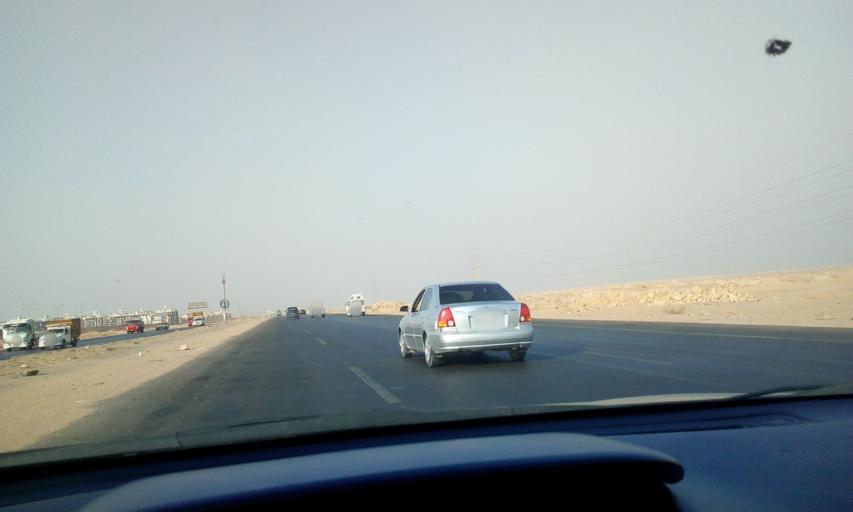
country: EG
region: Al Jizah
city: Madinat Sittah Uktubar
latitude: 29.8831
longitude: 31.0788
